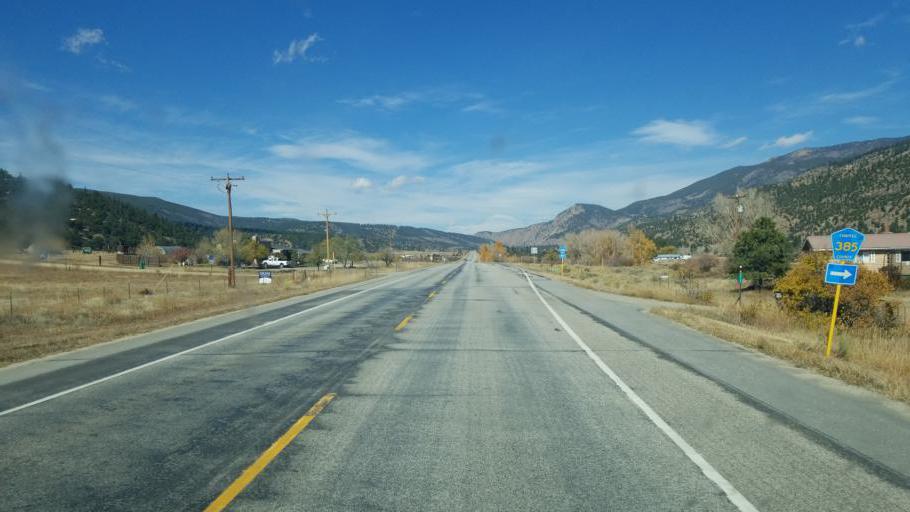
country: US
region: Colorado
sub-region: Chaffee County
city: Buena Vista
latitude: 38.9361
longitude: -106.1873
